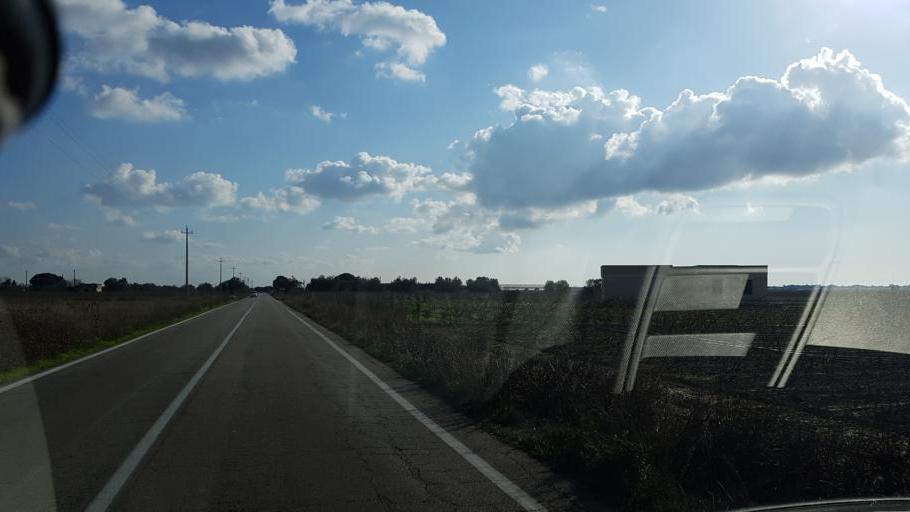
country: IT
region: Apulia
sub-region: Provincia di Lecce
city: Veglie
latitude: 40.3174
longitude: 17.9809
